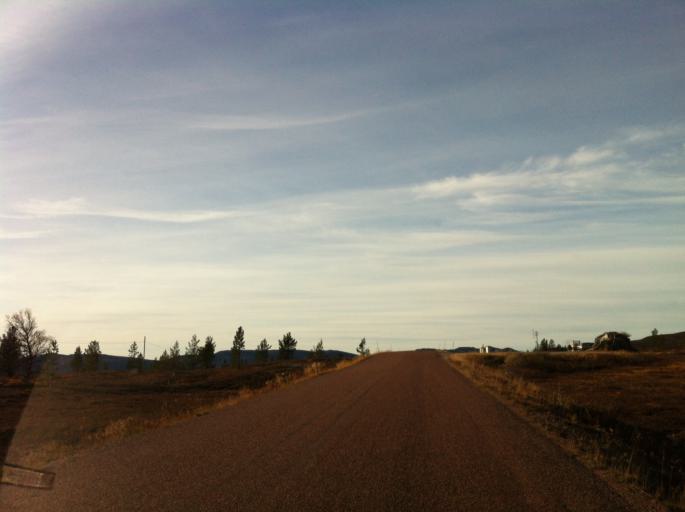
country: NO
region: Hedmark
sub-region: Engerdal
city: Engerdal
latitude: 62.0797
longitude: 12.1581
